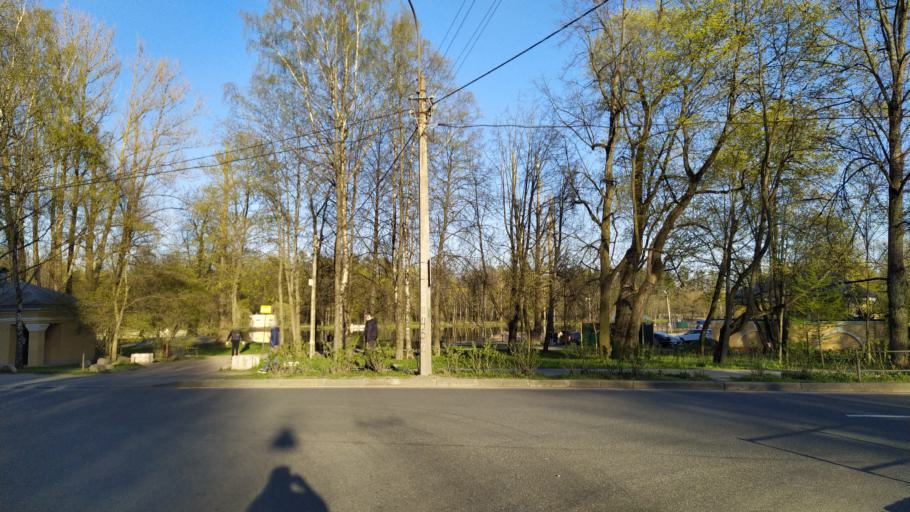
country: RU
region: St.-Petersburg
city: Pushkin
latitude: 59.7135
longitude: 30.4179
